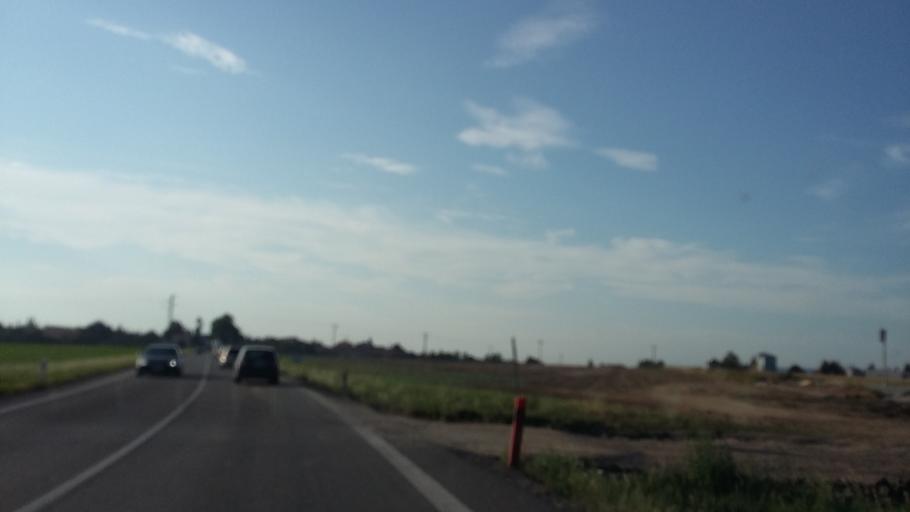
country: CZ
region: Central Bohemia
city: Lustenice
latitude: 50.3143
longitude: 14.9483
